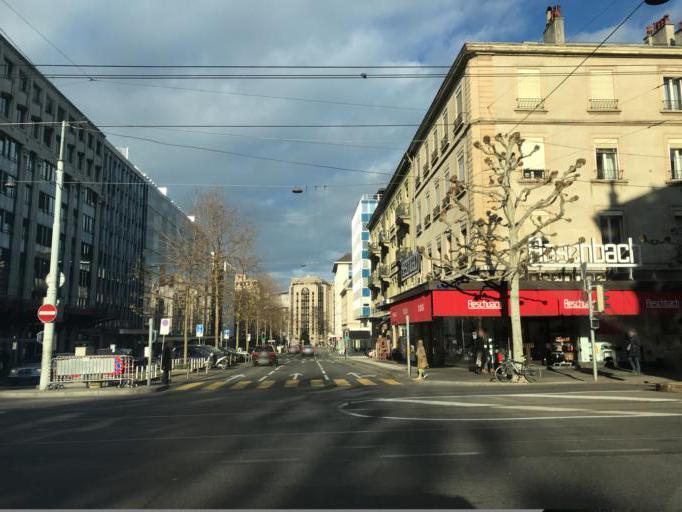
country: CH
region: Geneva
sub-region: Geneva
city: Geneve
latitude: 46.2012
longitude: 6.1547
